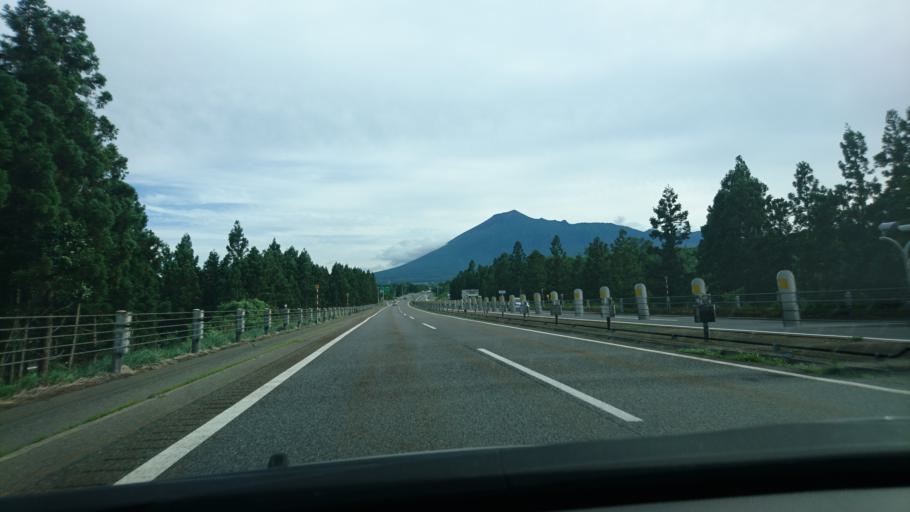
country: JP
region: Iwate
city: Shizukuishi
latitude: 39.9549
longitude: 141.0326
